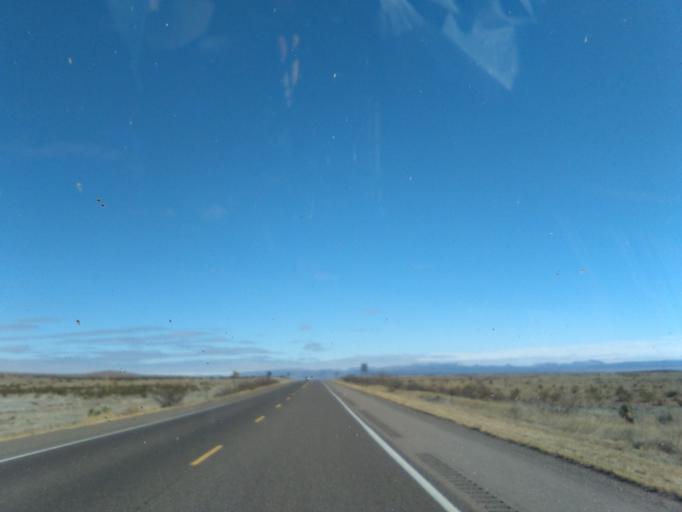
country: US
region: New Mexico
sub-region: Dona Ana County
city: Hatch
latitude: 32.5779
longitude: -107.4433
